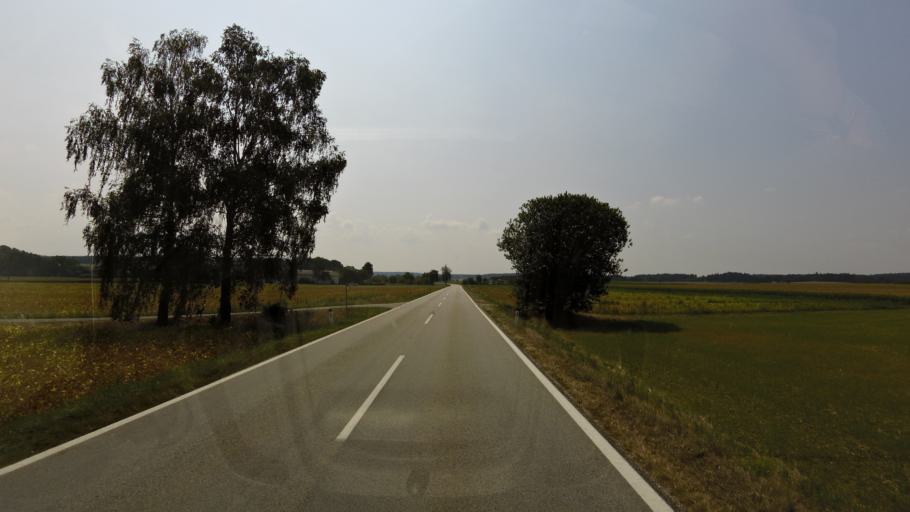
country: DE
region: Bavaria
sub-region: Lower Bavaria
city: Bad Fussing
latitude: 48.2763
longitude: 13.3291
